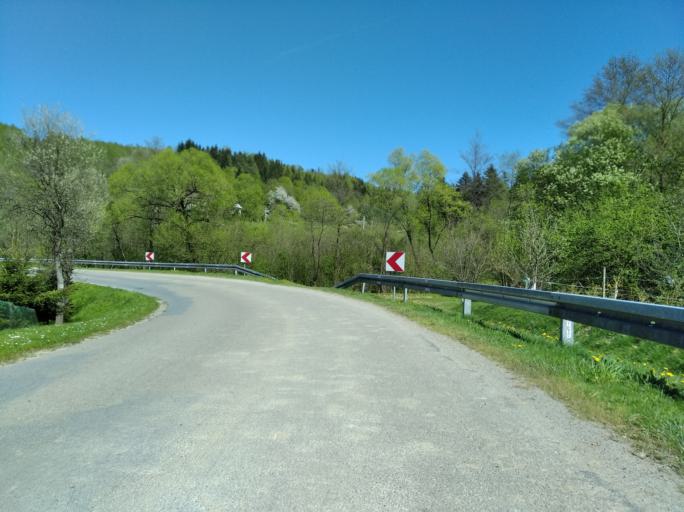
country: PL
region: Subcarpathian Voivodeship
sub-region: Powiat strzyzowski
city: Frysztak
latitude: 49.8662
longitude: 21.5598
